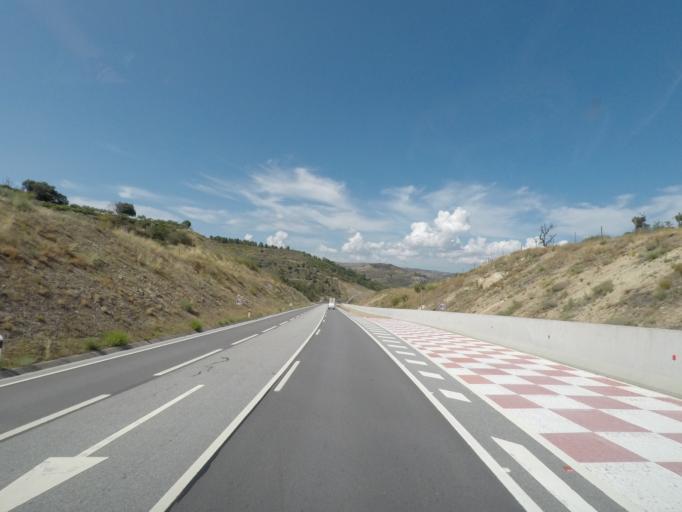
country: PT
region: Braganca
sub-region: Carrazeda de Ansiaes
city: Carrazeda de Anciaes
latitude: 41.3164
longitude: -7.3530
